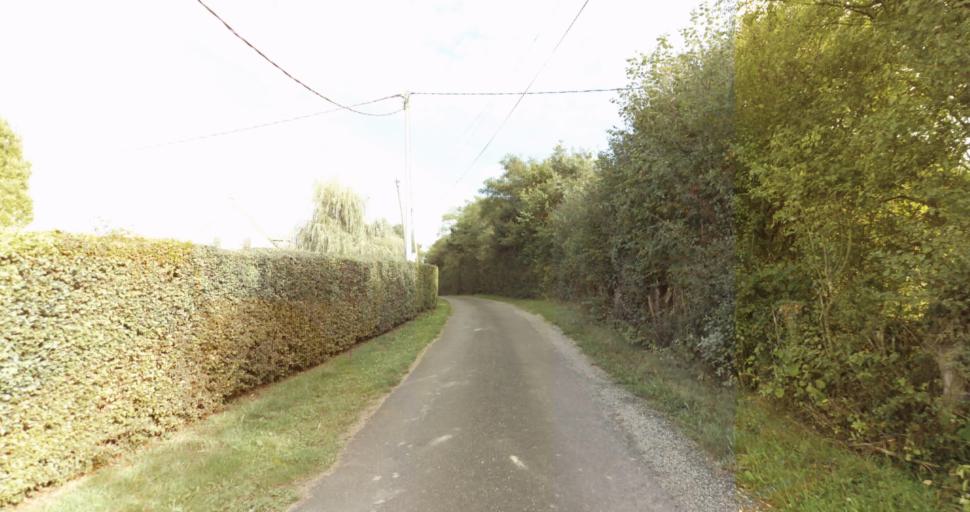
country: FR
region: Lower Normandy
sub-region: Departement de l'Orne
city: Gace
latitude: 48.7002
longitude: 0.3032
